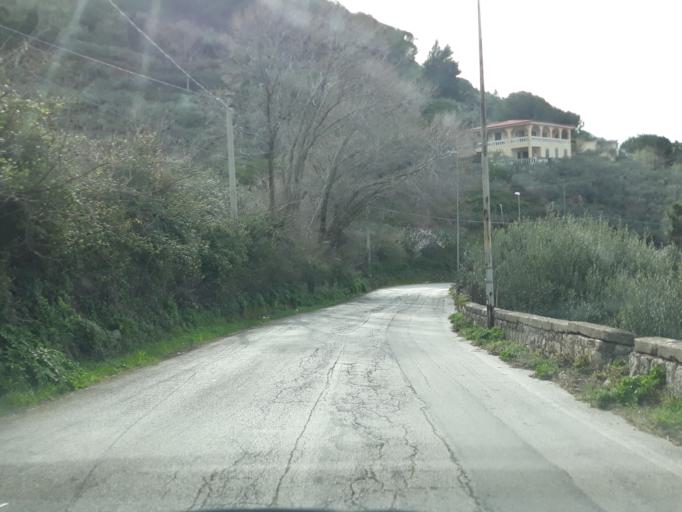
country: IT
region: Sicily
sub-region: Palermo
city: Altofonte
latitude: 38.0413
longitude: 13.3014
